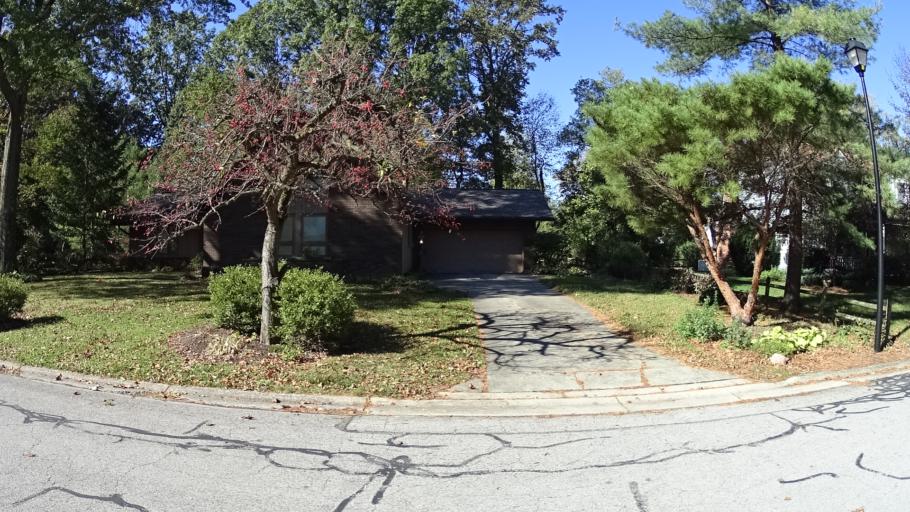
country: US
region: Ohio
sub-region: Lorain County
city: Oberlin
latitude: 41.2897
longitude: -82.2340
